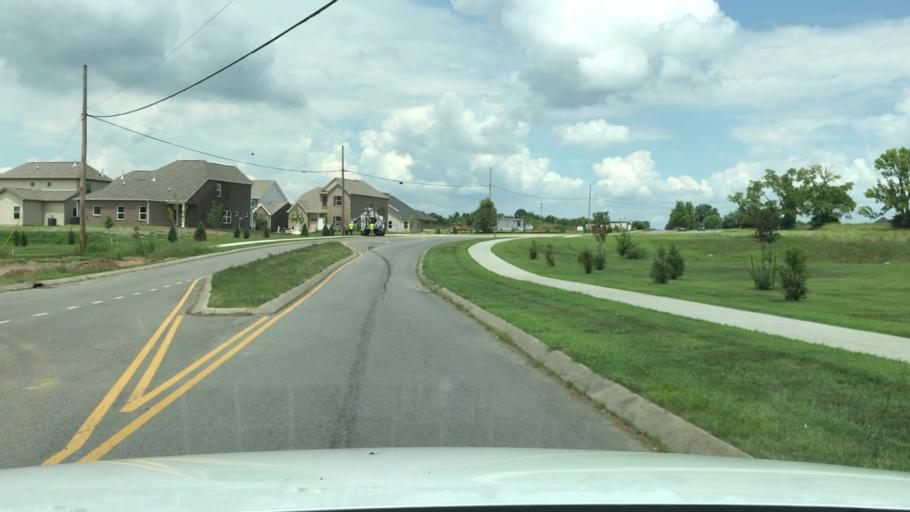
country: US
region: Tennessee
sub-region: Sumner County
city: Gallatin
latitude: 36.3595
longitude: -86.4479
